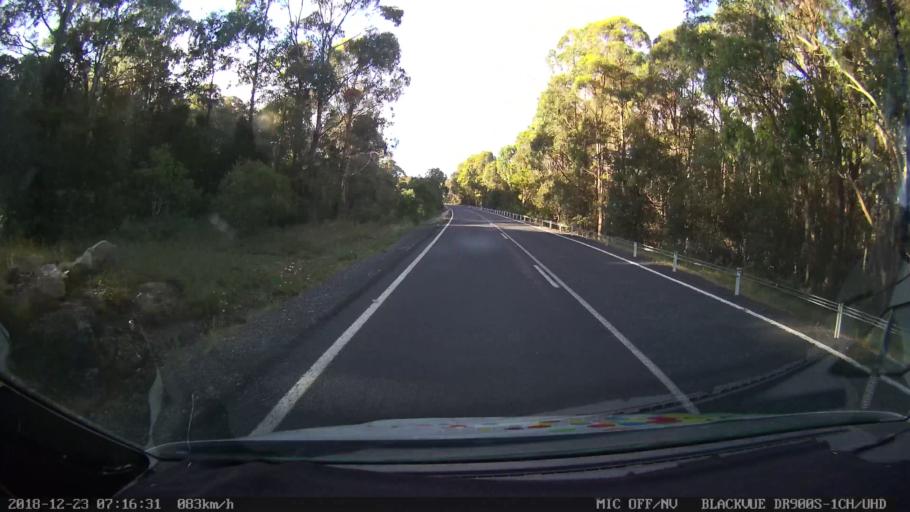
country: AU
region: New South Wales
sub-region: Bellingen
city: Dorrigo
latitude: -30.4567
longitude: 152.3089
